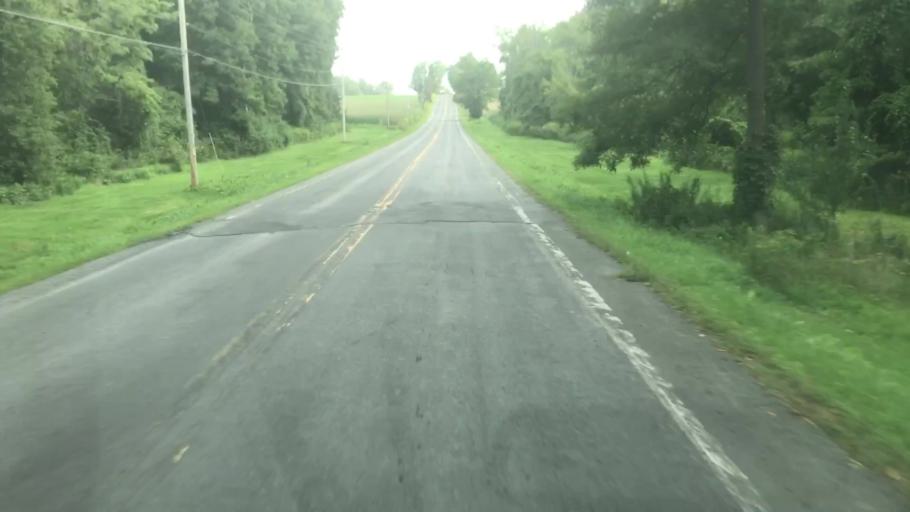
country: US
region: New York
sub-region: Onondaga County
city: Skaneateles
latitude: 42.8696
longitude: -76.4480
